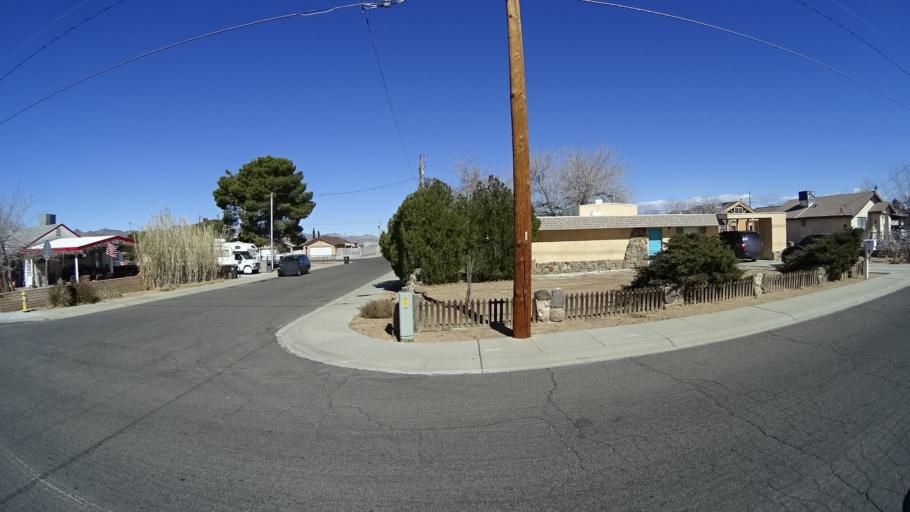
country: US
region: Arizona
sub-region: Mohave County
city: Kingman
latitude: 35.1993
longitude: -114.0180
